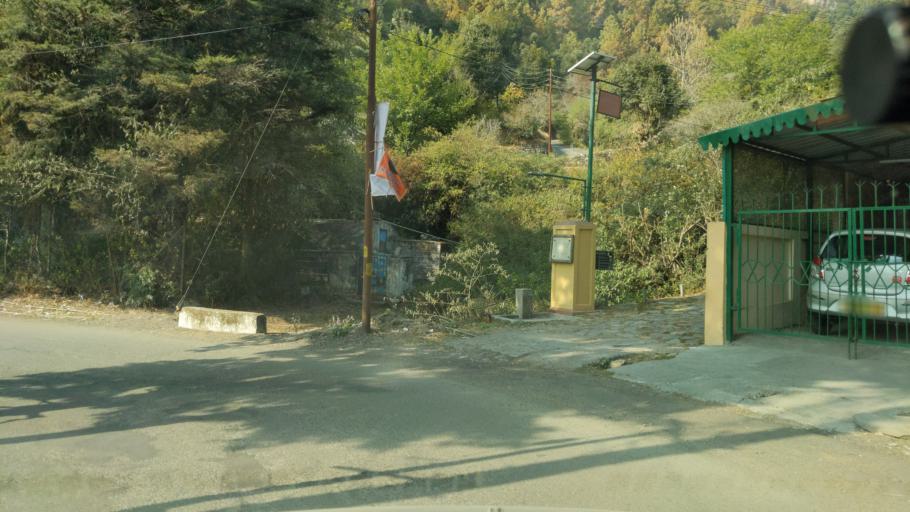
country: IN
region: Uttarakhand
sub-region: Naini Tal
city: Bhowali
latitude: 29.3923
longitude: 79.5332
